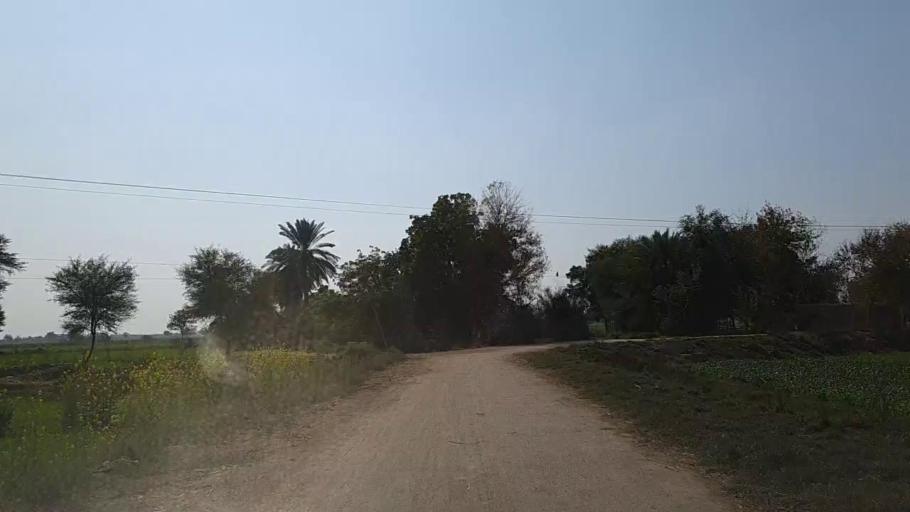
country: PK
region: Sindh
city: Nawabshah
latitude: 26.2478
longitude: 68.4842
